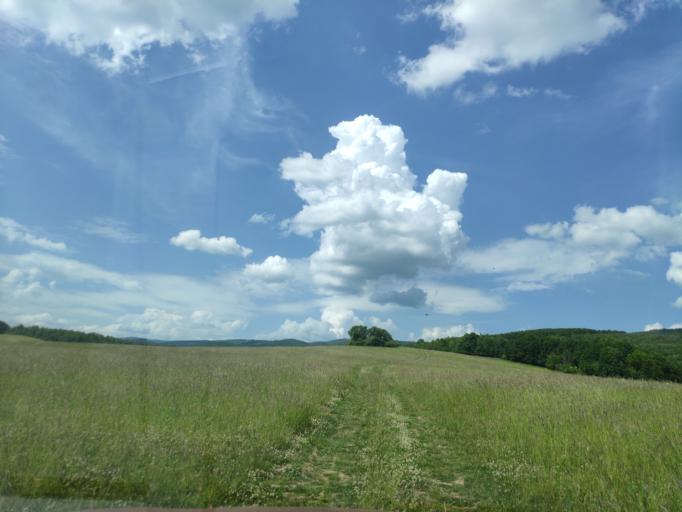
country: SK
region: Kosicky
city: Medzev
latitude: 48.7163
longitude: 20.9629
